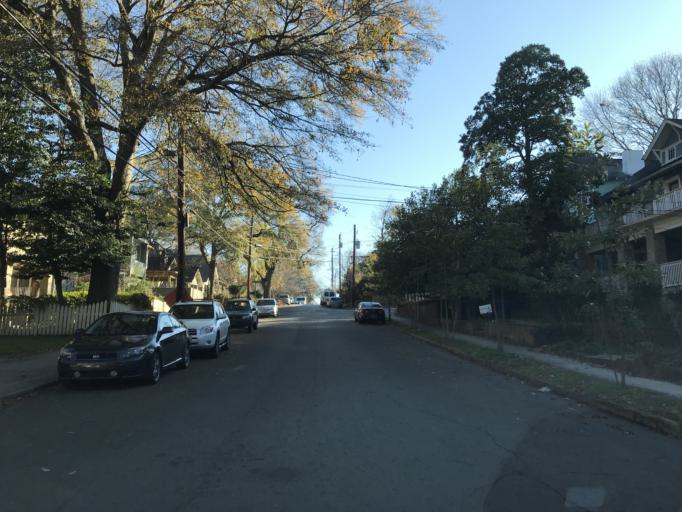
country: US
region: Georgia
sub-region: Fulton County
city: Atlanta
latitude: 33.7744
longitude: -84.3765
